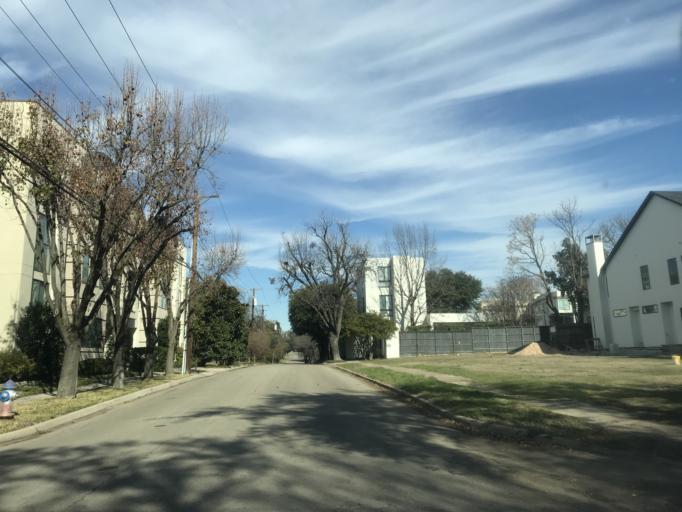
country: US
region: Texas
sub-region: Dallas County
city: Highland Park
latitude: 32.8190
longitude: -96.7961
